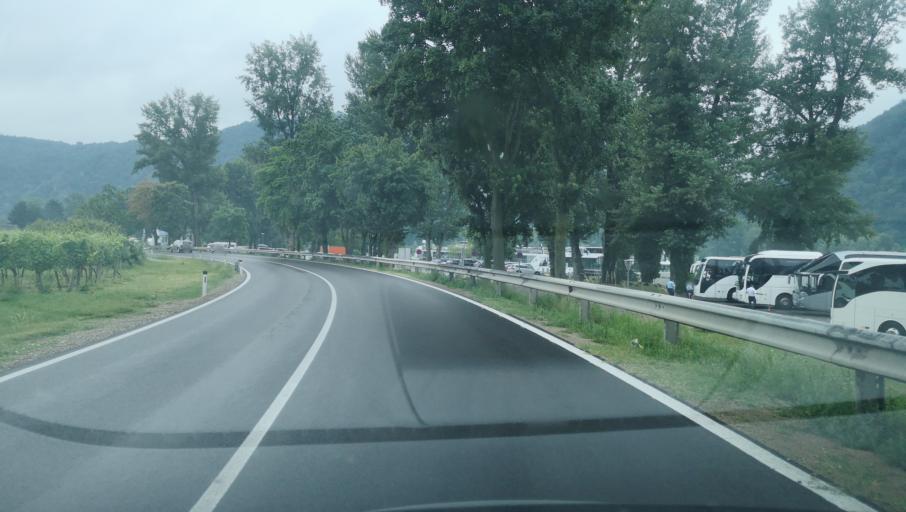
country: AT
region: Lower Austria
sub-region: Politischer Bezirk Krems
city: Durnstein
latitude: 48.3905
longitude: 15.5225
